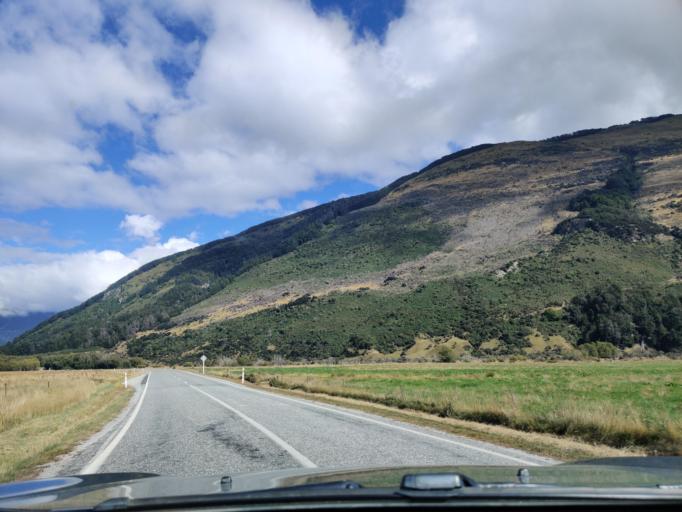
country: NZ
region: Otago
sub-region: Queenstown-Lakes District
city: Queenstown
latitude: -44.7831
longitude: 168.3941
